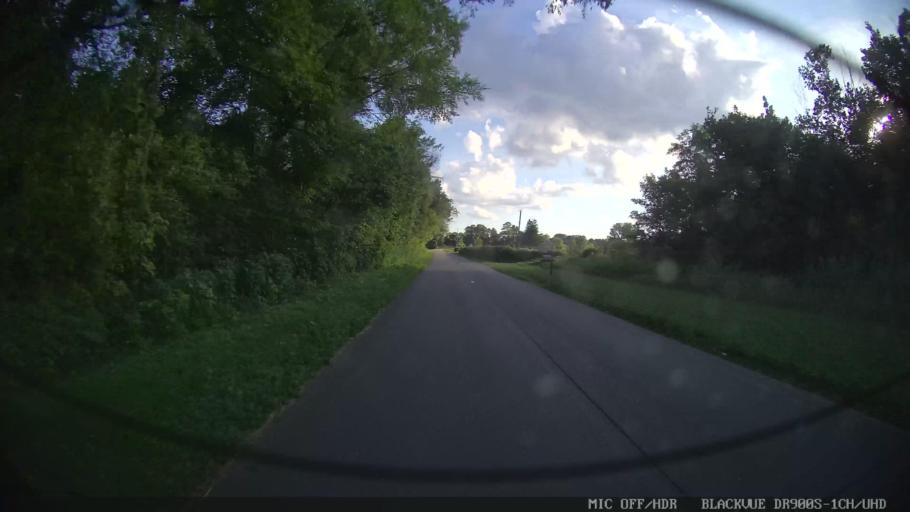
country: US
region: Georgia
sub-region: Bartow County
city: Rydal
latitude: 34.2924
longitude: -84.7400
